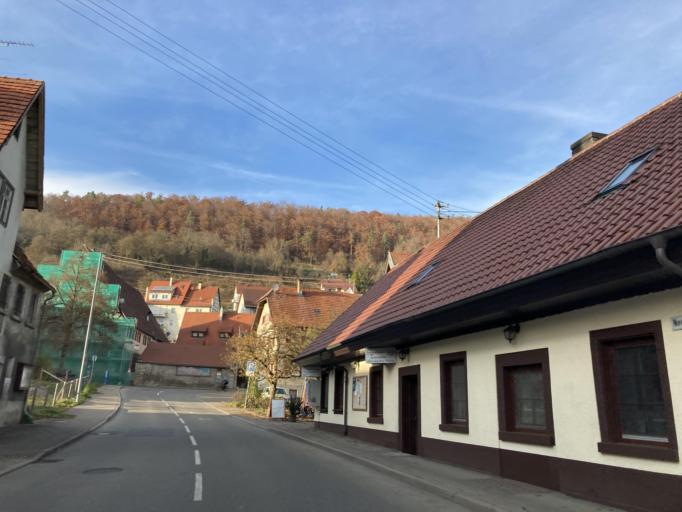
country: DE
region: Baden-Wuerttemberg
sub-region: Tuebingen Region
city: Hirrlingen
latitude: 48.4513
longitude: 8.8564
